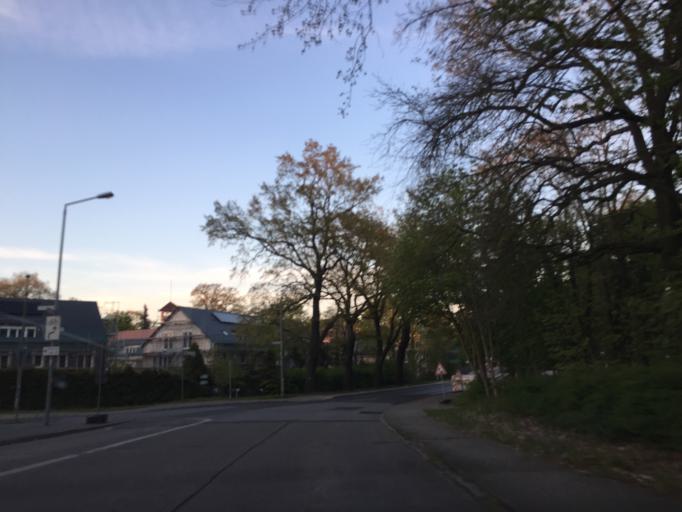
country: DE
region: Brandenburg
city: Potsdam
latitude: 52.3827
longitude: 13.0444
